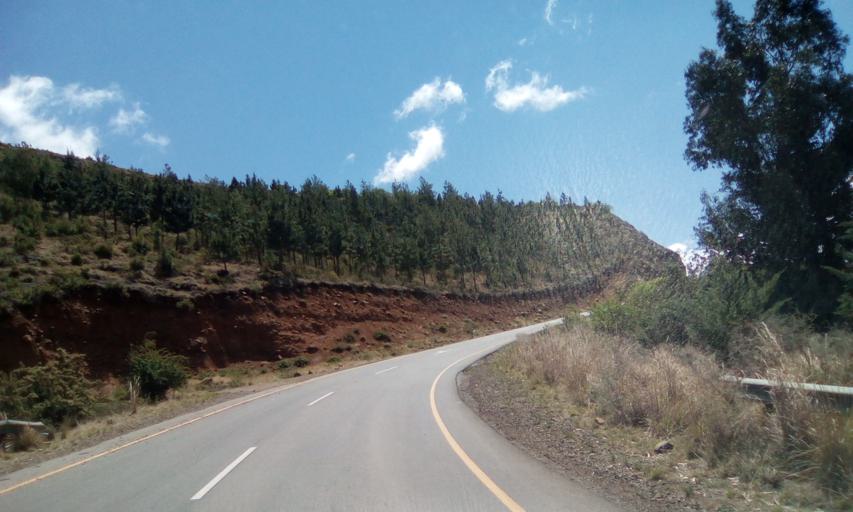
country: LS
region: Qacha's Nek
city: Qacha's Nek
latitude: -30.0778
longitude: 28.6206
